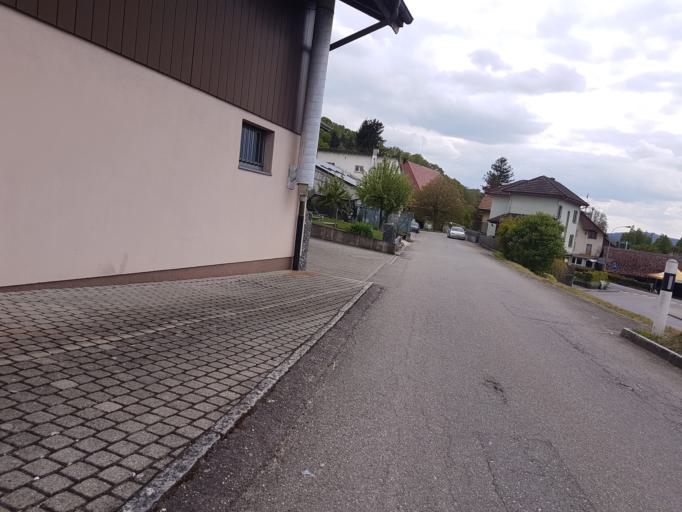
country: CH
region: Bern
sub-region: Seeland District
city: Arch
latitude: 47.1660
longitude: 7.4313
